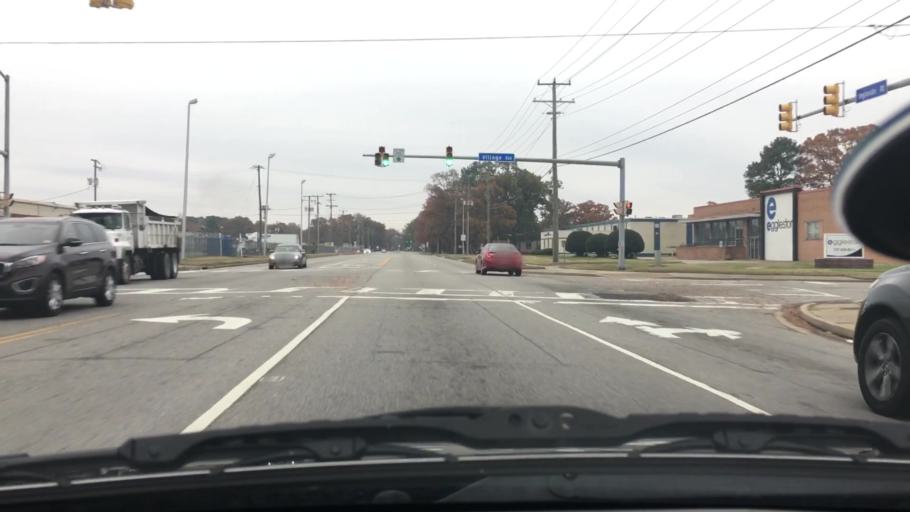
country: US
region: Virginia
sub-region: City of Norfolk
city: Norfolk
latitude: 36.8589
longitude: -76.2424
